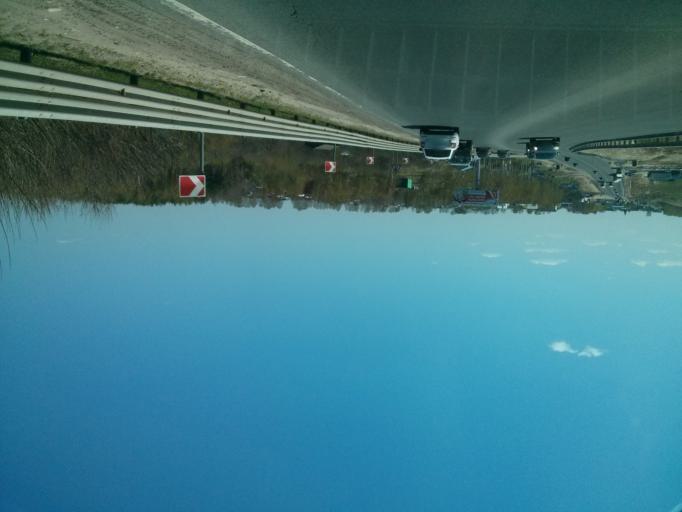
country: RU
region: Nizjnij Novgorod
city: Burevestnik
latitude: 56.2149
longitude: 43.9082
